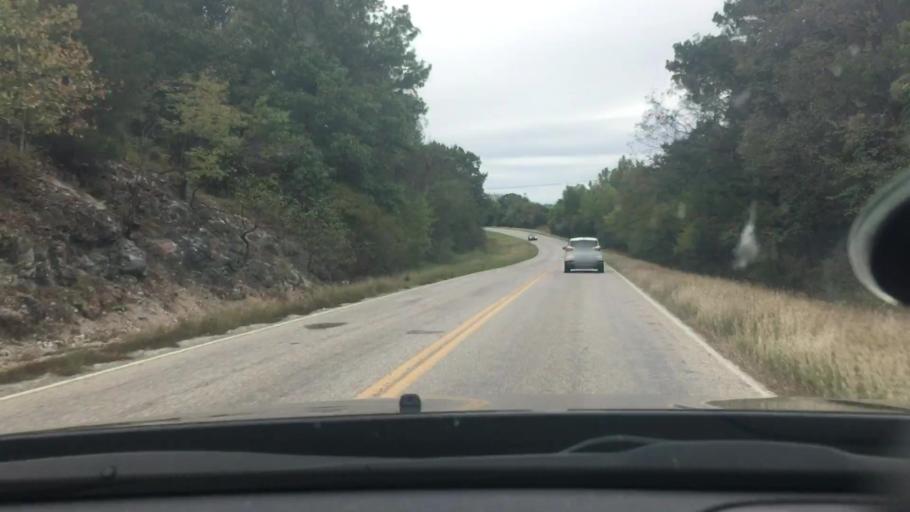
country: US
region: Oklahoma
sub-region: Johnston County
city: Tishomingo
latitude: 34.3323
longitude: -96.4195
